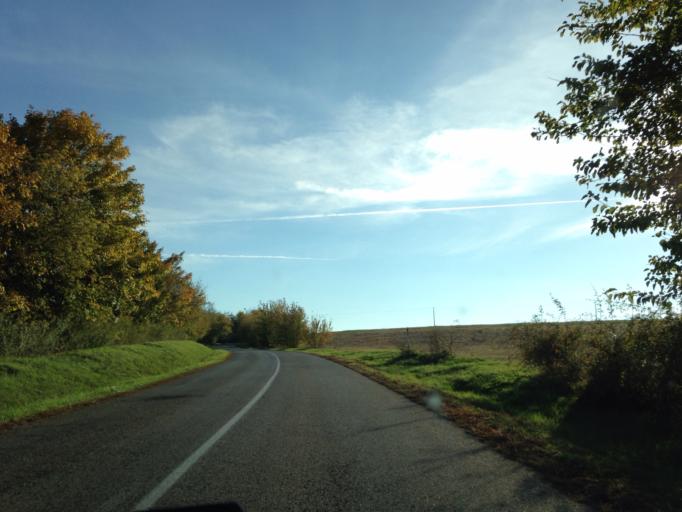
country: SK
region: Nitriansky
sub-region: Okres Komarno
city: Hurbanovo
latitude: 47.8782
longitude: 18.2864
